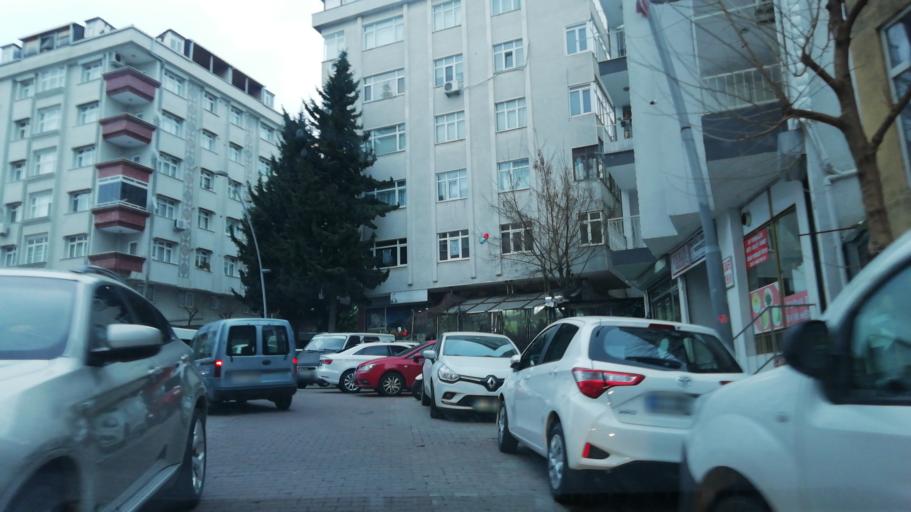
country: TR
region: Istanbul
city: Bahcelievler
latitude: 41.0004
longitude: 28.8546
